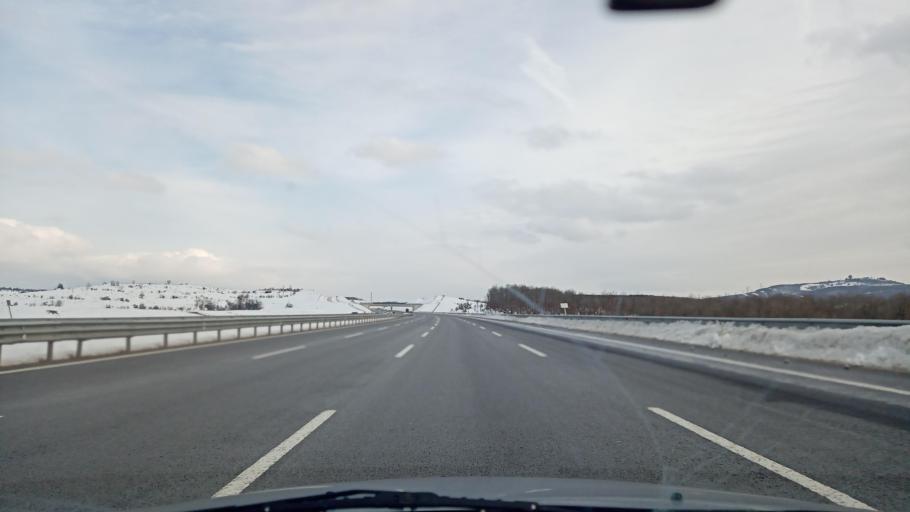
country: TR
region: Kocaeli
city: Hereke
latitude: 40.8940
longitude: 29.6168
